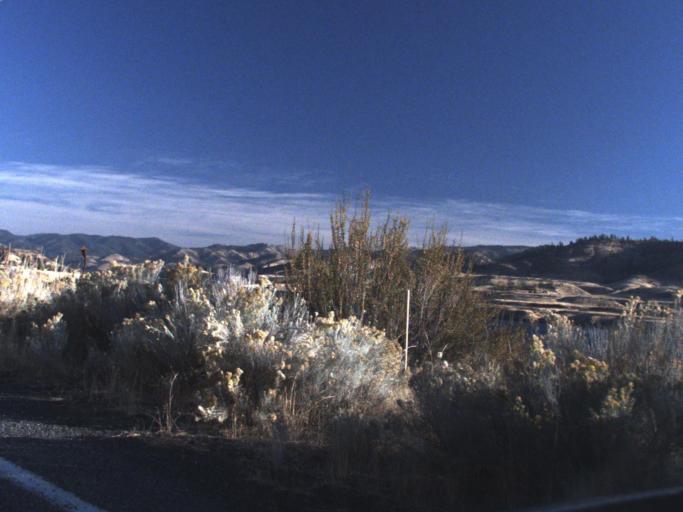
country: US
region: Washington
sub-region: Okanogan County
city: Coulee Dam
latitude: 47.9692
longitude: -118.6993
